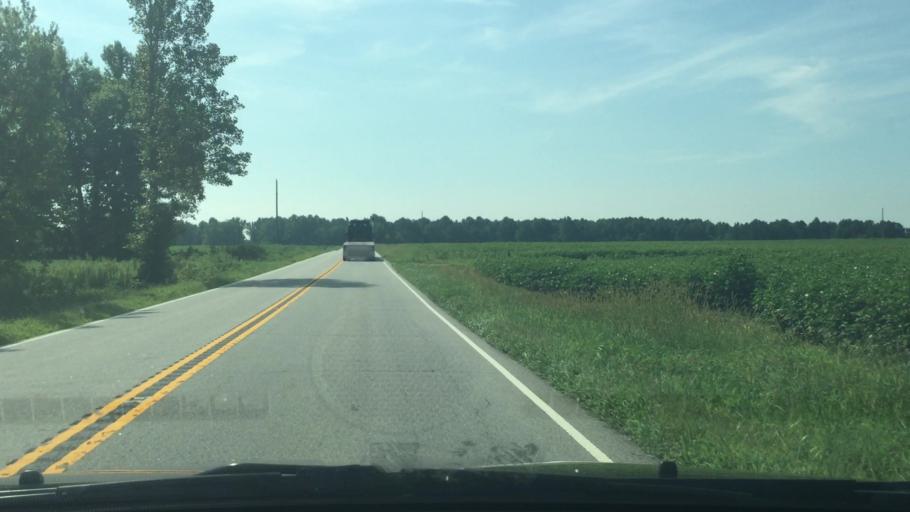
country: US
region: Virginia
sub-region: Sussex County
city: Sussex
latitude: 36.8766
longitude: -77.1493
